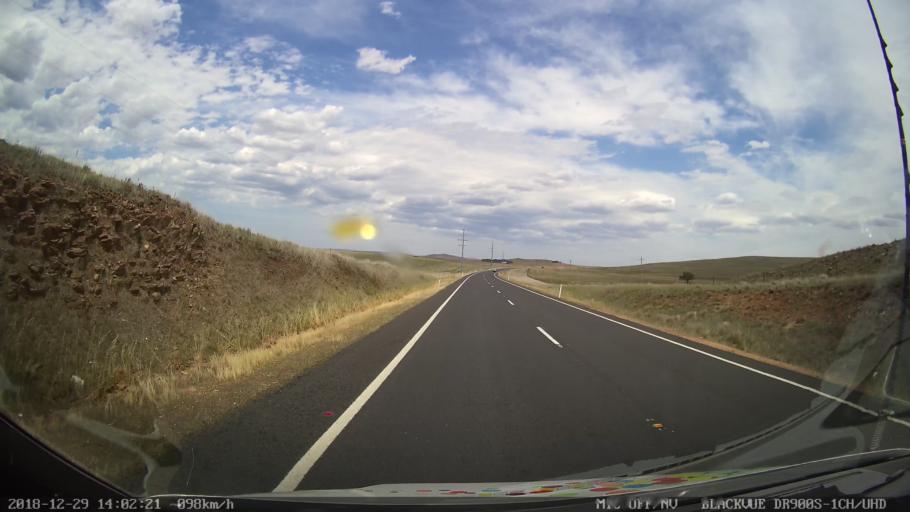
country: AU
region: New South Wales
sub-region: Cooma-Monaro
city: Cooma
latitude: -36.2869
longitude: 149.1763
